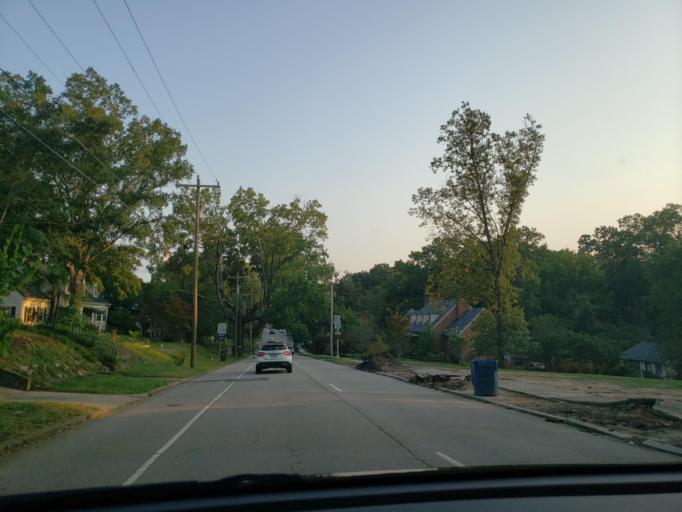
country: US
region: North Carolina
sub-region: Durham County
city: Durham
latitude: 36.0147
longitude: -78.9083
